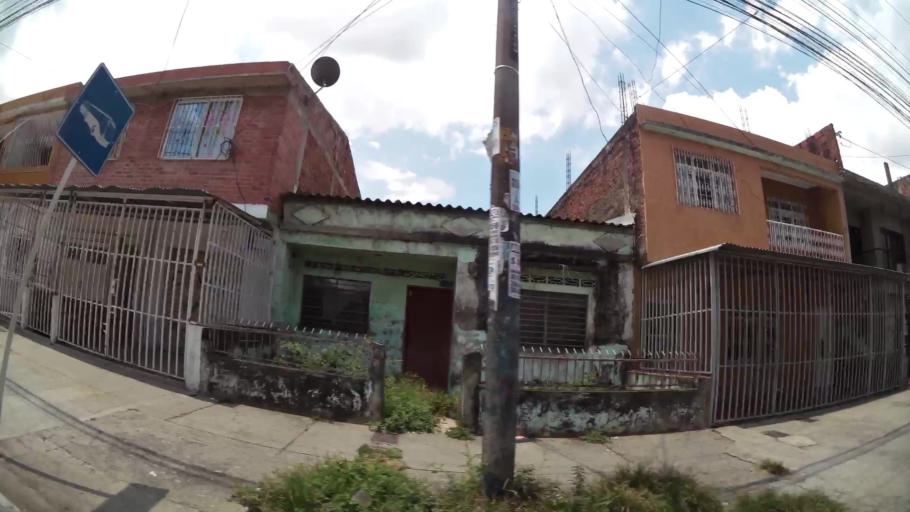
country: CO
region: Valle del Cauca
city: Cali
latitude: 3.4516
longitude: -76.4807
